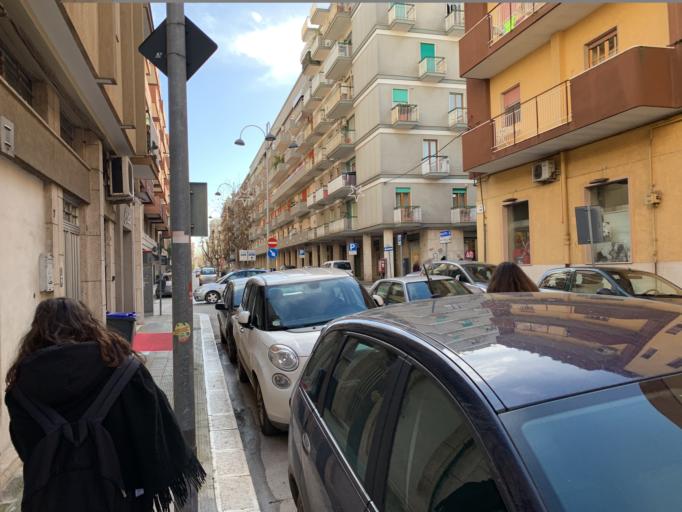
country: IT
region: Apulia
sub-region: Provincia di Barletta - Andria - Trani
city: Andria
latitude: 41.2307
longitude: 16.2988
